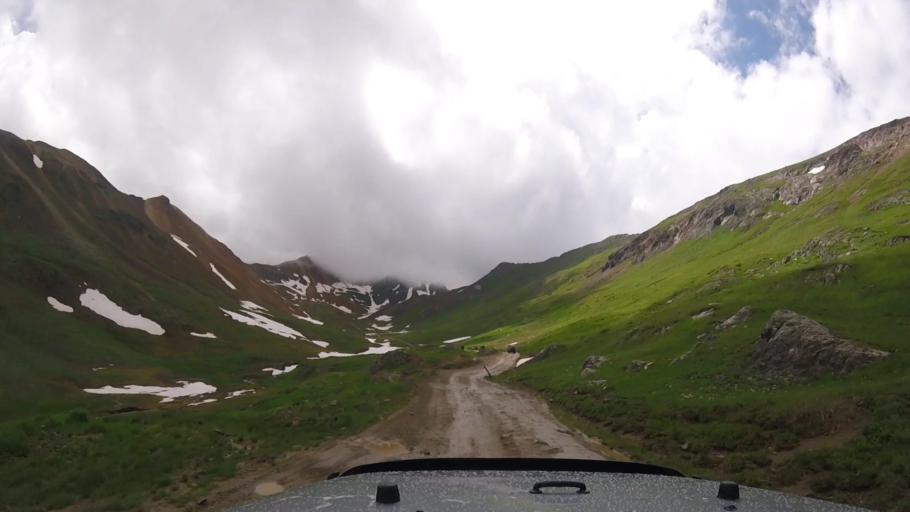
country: US
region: Colorado
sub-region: Ouray County
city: Ouray
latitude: 37.9268
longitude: -107.6090
